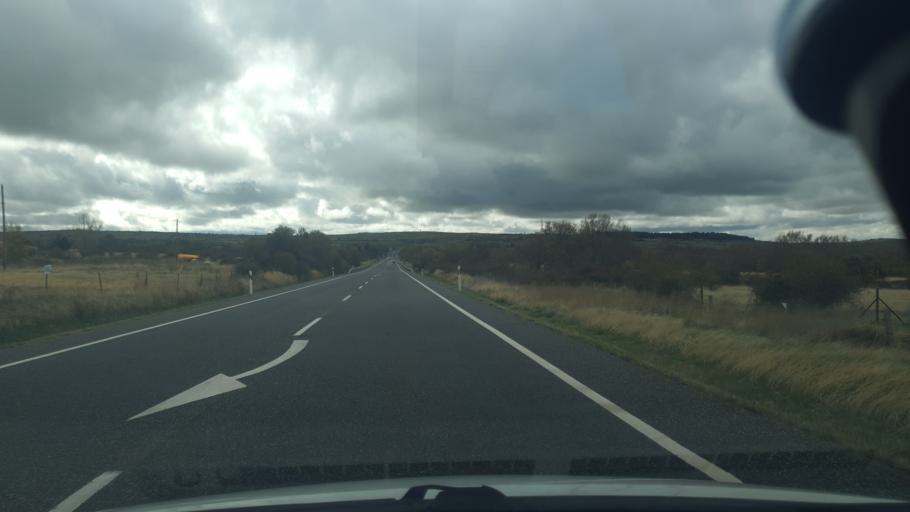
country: ES
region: Castille and Leon
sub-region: Provincia de Segovia
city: Santo Domingo de Piron
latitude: 41.0157
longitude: -3.9732
